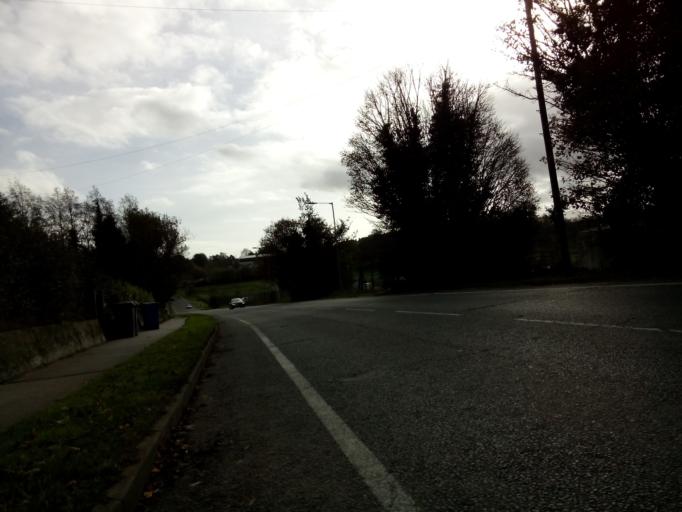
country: GB
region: England
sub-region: Suffolk
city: Ipswich
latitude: 52.0426
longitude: 1.1662
